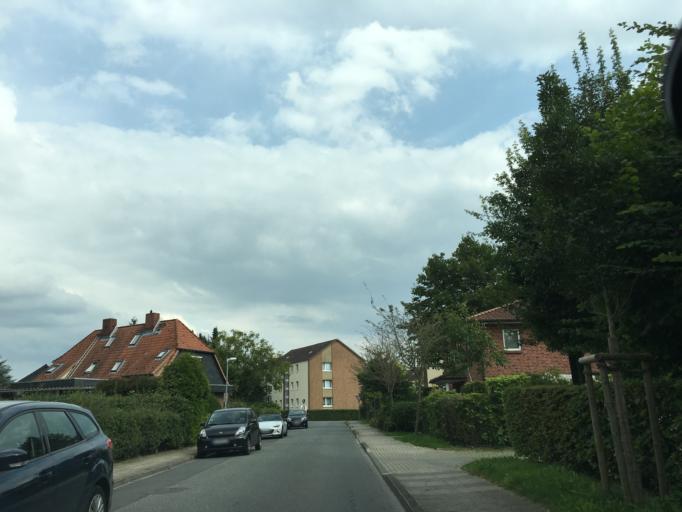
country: DE
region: Lower Saxony
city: Lueneburg
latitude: 53.2569
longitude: 10.3853
